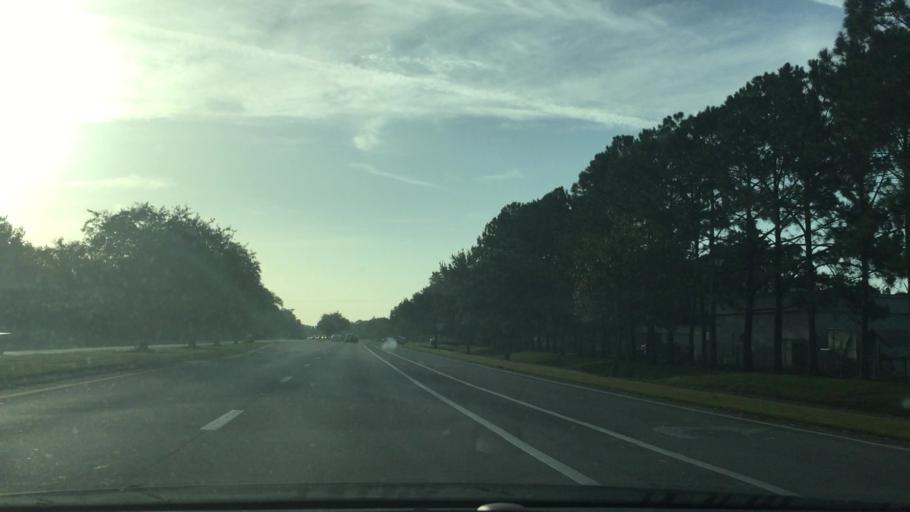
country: US
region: Florida
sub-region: Orange County
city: Pine Hills
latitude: 28.5708
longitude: -81.4283
